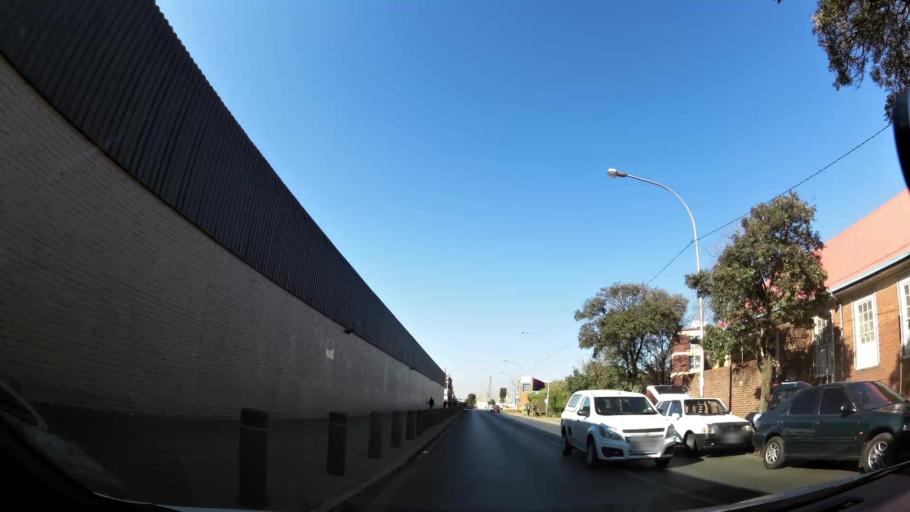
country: ZA
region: Gauteng
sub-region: Ekurhuleni Metropolitan Municipality
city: Germiston
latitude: -26.2037
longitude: 28.1159
